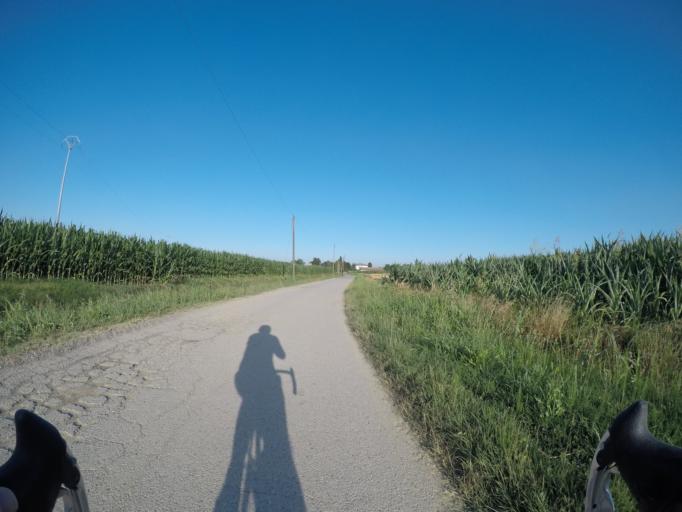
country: IT
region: Veneto
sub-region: Provincia di Rovigo
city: Villamarzana
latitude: 45.0261
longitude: 11.6728
